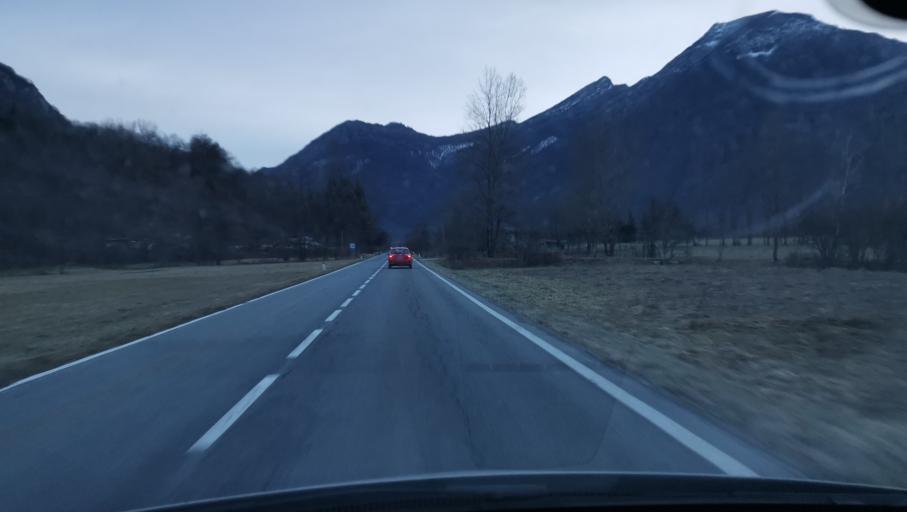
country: IT
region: Piedmont
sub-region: Provincia di Cuneo
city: Valloriate
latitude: 44.3125
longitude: 7.3477
